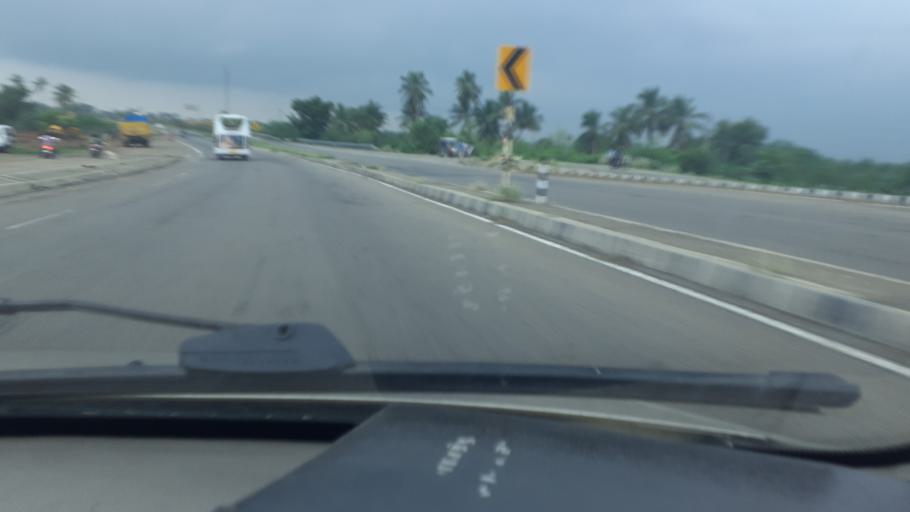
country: IN
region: Tamil Nadu
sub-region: Thoothukkudi
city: Kovilpatti
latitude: 9.1351
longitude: 77.8256
